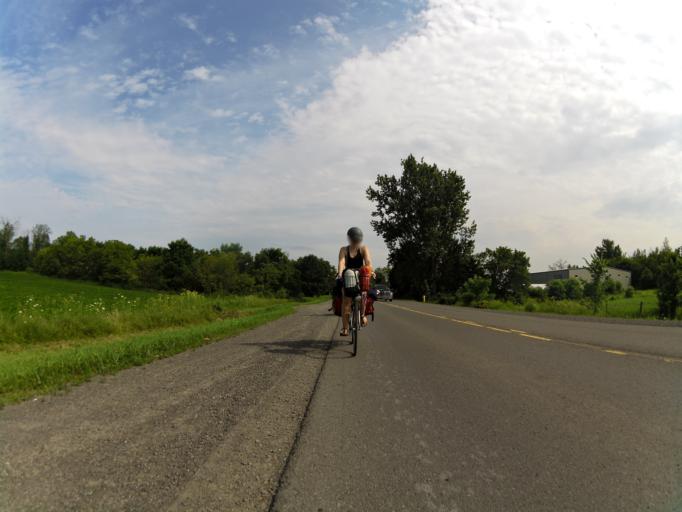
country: CA
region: Ontario
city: Prescott
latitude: 45.0221
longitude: -75.6325
